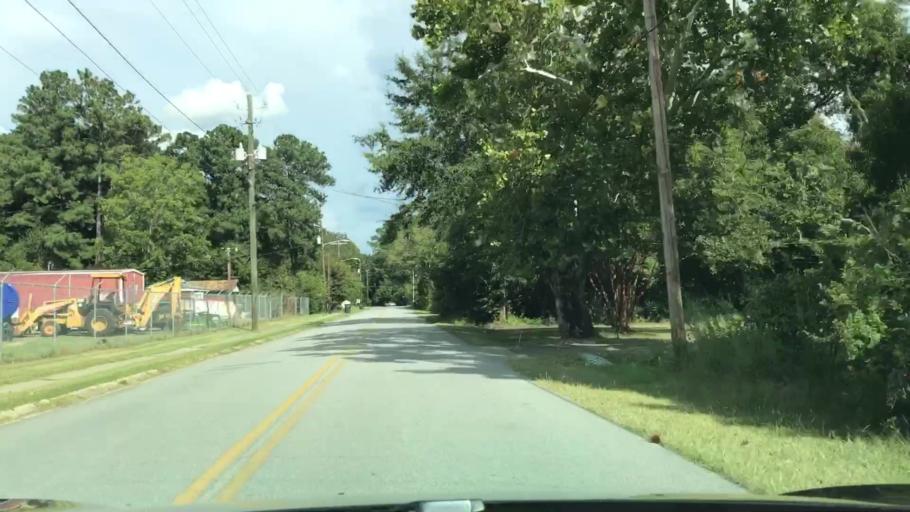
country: US
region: Georgia
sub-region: Jefferson County
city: Wadley
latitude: 32.8629
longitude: -82.4004
